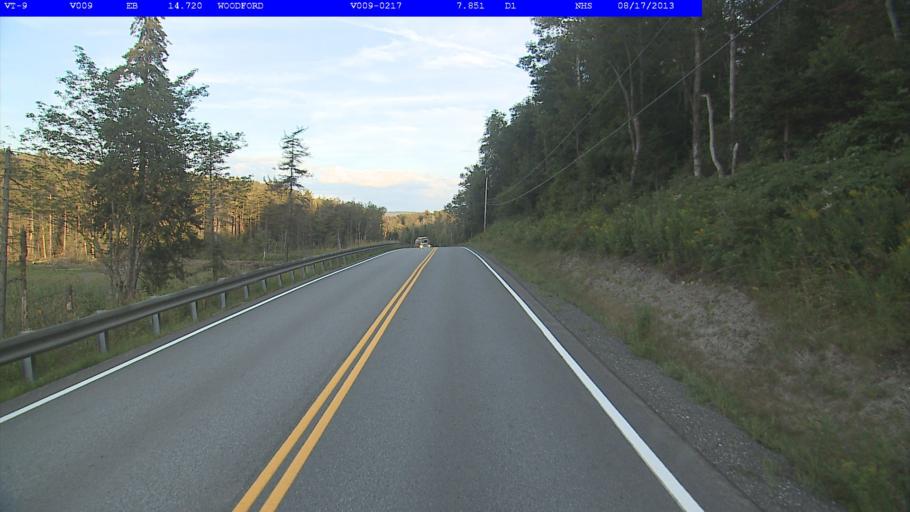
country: US
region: Vermont
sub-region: Bennington County
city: Bennington
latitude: 42.8958
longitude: -73.0414
